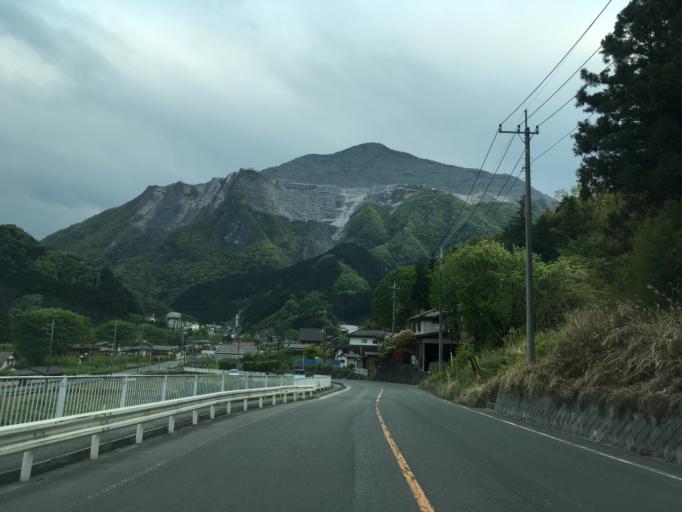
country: JP
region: Saitama
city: Chichibu
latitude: 35.9765
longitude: 139.1059
